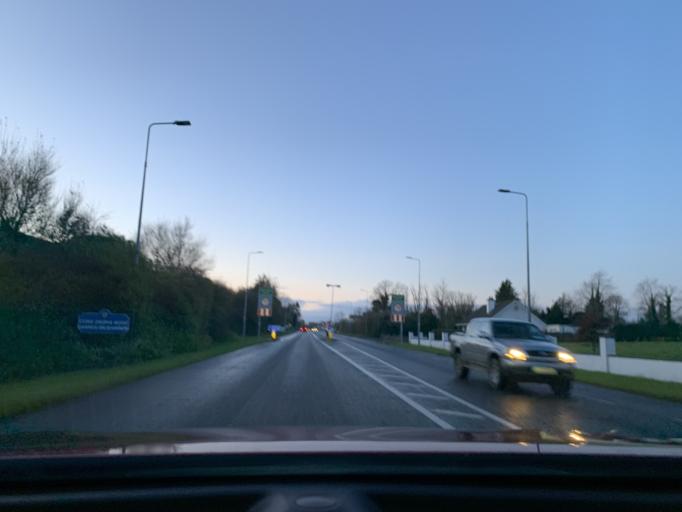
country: IE
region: Connaught
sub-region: County Leitrim
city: Carrick-on-Shannon
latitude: 53.9419
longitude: -8.0673
